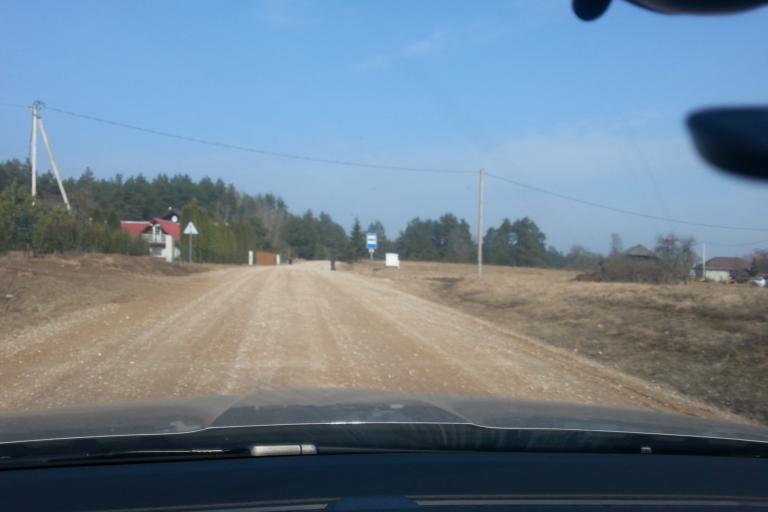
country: LT
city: Trakai
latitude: 54.5704
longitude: 24.9677
